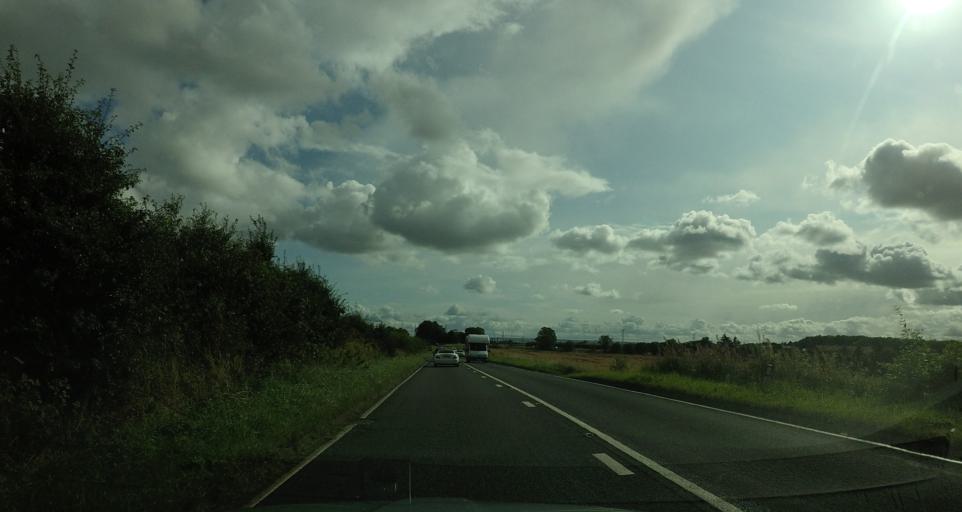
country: GB
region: Scotland
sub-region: Clackmannanshire
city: Clackmannan
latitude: 56.1023
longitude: -3.7176
